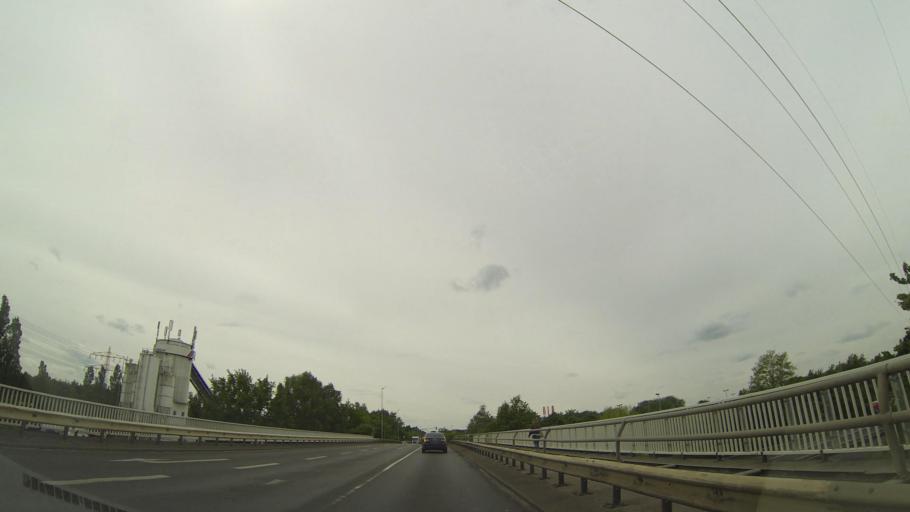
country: DE
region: Schleswig-Holstein
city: Ellerbek
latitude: 53.6291
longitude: 9.8709
